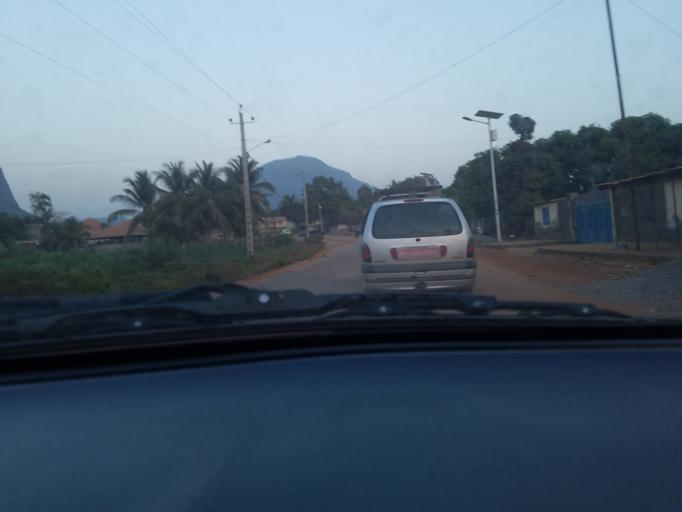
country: GN
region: Kindia
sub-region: Prefecture de Dubreka
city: Dubreka
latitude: 9.7885
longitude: -13.5007
